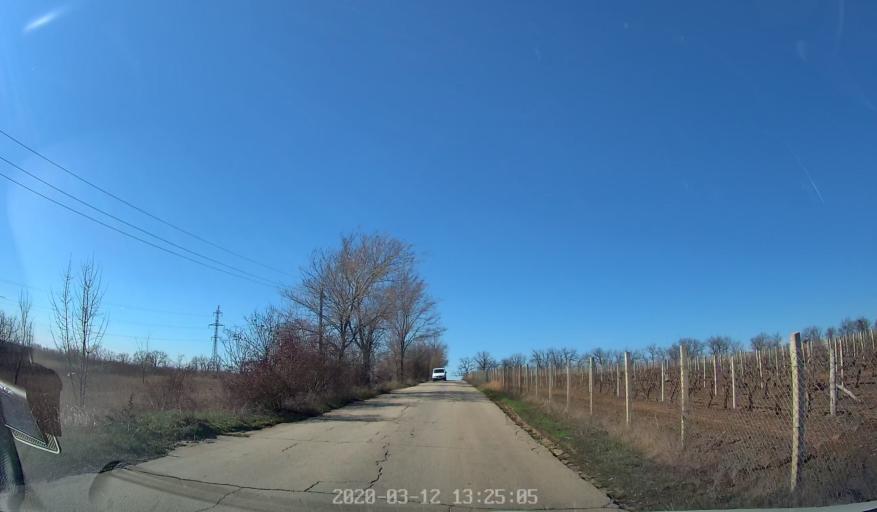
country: MD
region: Laloveni
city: Ialoveni
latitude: 46.9420
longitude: 28.8223
